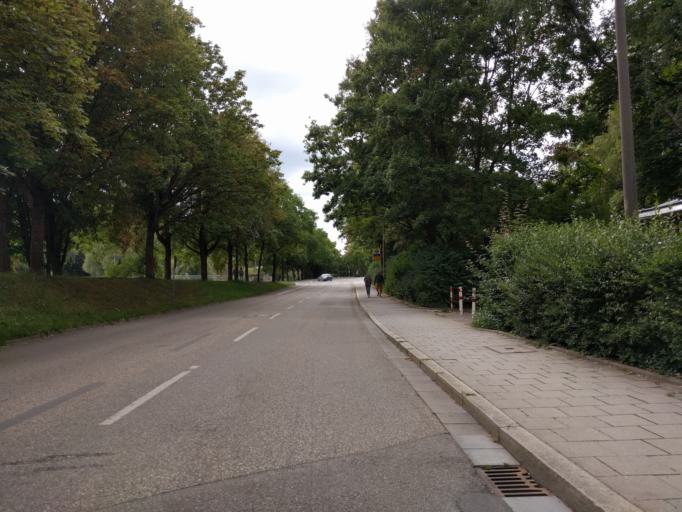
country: DE
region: Bavaria
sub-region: Upper Palatinate
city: Lappersdorf
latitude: 49.0250
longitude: 12.0917
